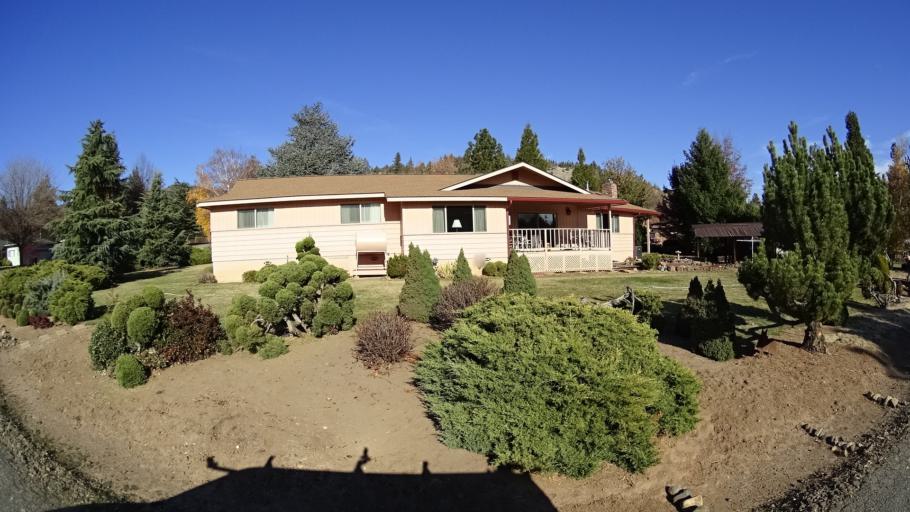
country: US
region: California
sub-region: Siskiyou County
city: Yreka
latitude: 41.6914
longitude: -122.6528
